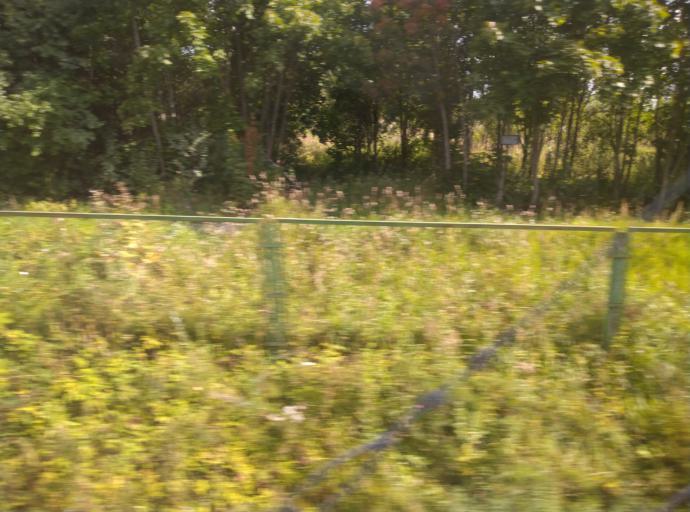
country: RU
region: Leningrad
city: Krasnyy Bor
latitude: 59.6832
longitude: 30.6969
